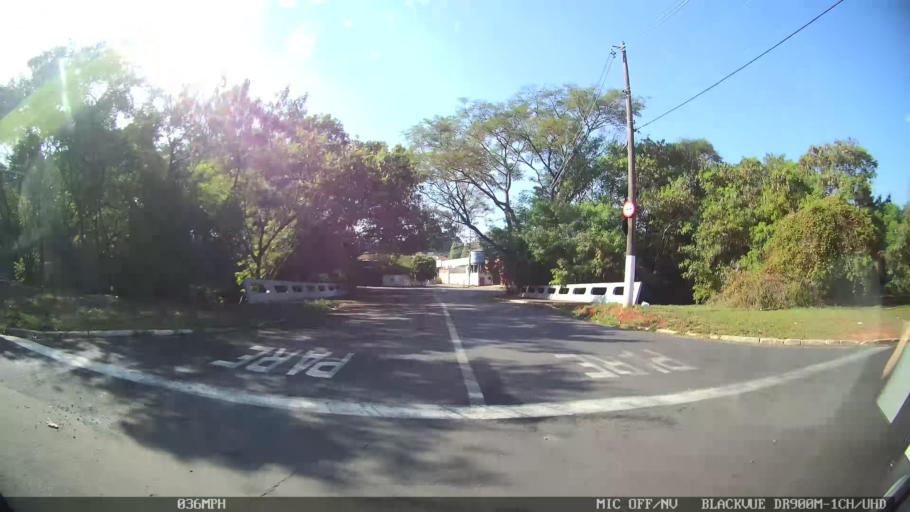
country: BR
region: Sao Paulo
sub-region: Americana
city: Americana
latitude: -22.7322
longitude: -47.3300
